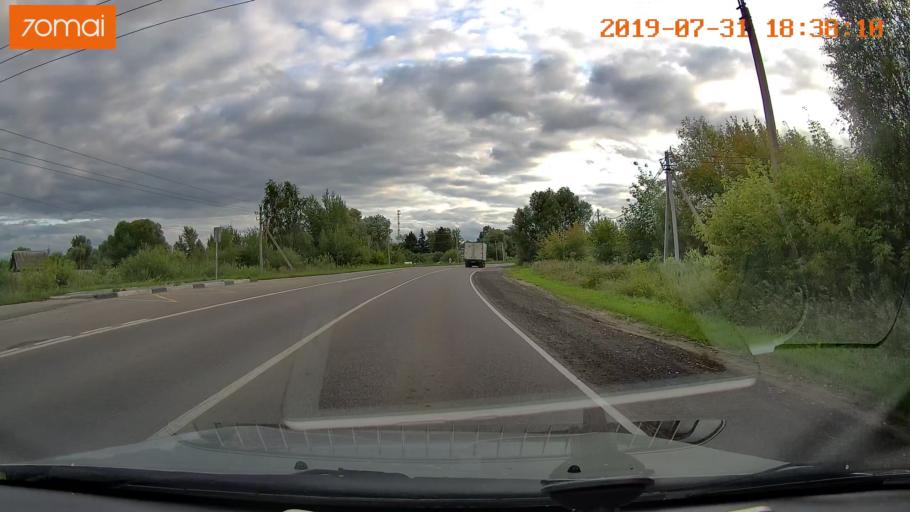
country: RU
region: Moskovskaya
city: Voskresensk
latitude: 55.2734
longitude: 38.6573
